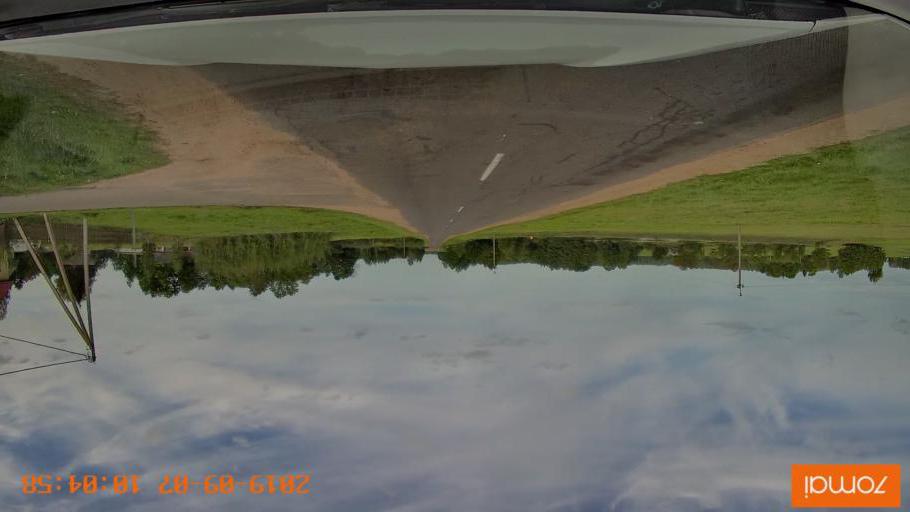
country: BY
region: Grodnenskaya
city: Voranava
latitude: 54.0415
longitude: 25.4096
